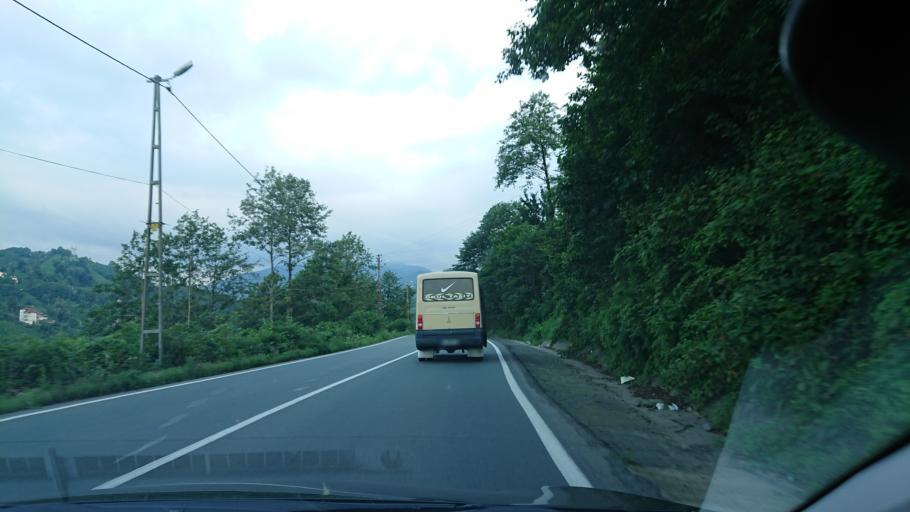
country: TR
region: Rize
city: Cayeli
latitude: 41.0687
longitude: 40.7131
